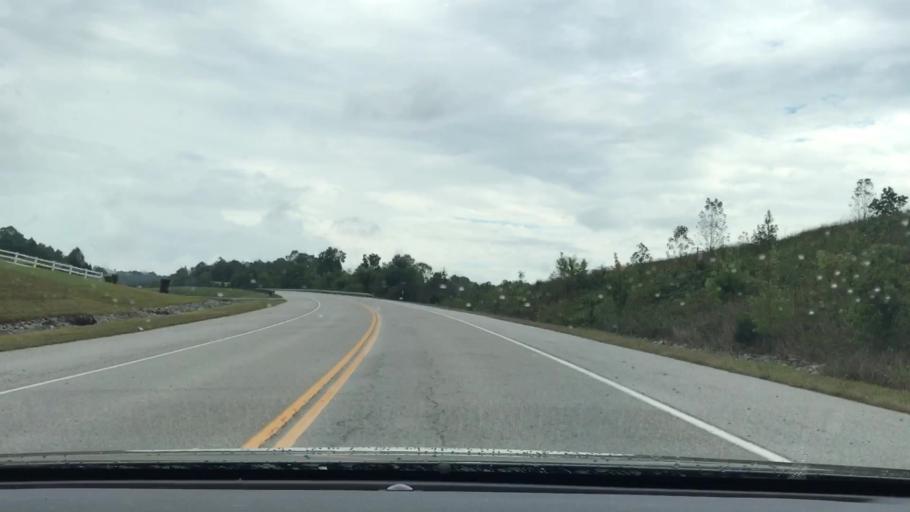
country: US
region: Tennessee
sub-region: Macon County
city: Red Boiling Springs
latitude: 36.5248
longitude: -85.8312
